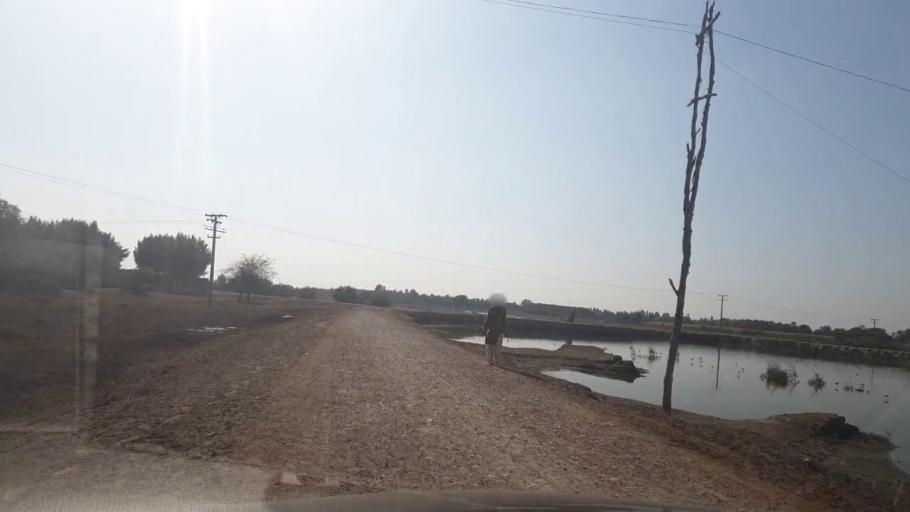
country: PK
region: Sindh
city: Khairpur
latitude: 28.1435
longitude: 69.6035
